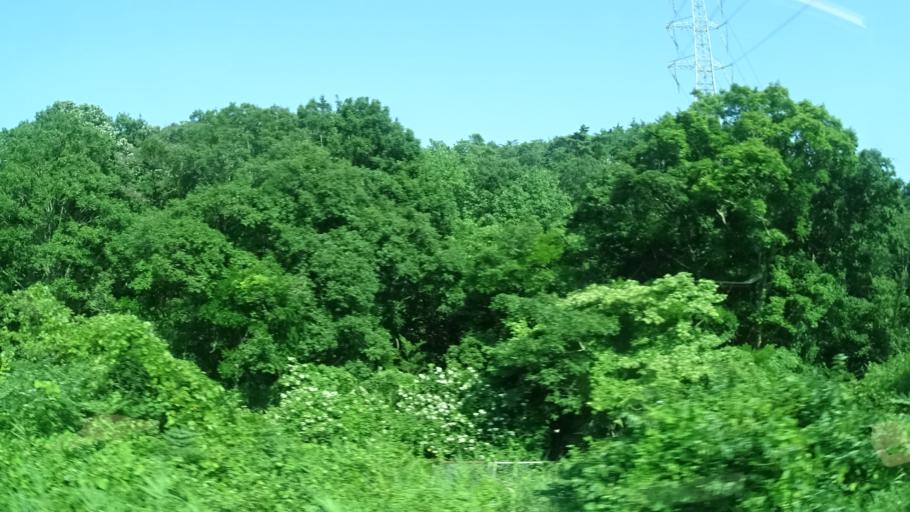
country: JP
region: Fukushima
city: Iwaki
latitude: 37.2396
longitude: 141.0074
